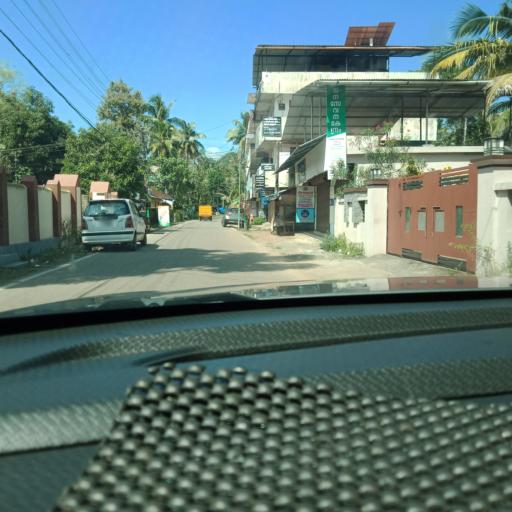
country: IN
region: Kerala
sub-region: Alappuzha
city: Mavelikara
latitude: 9.2849
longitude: 76.4568
